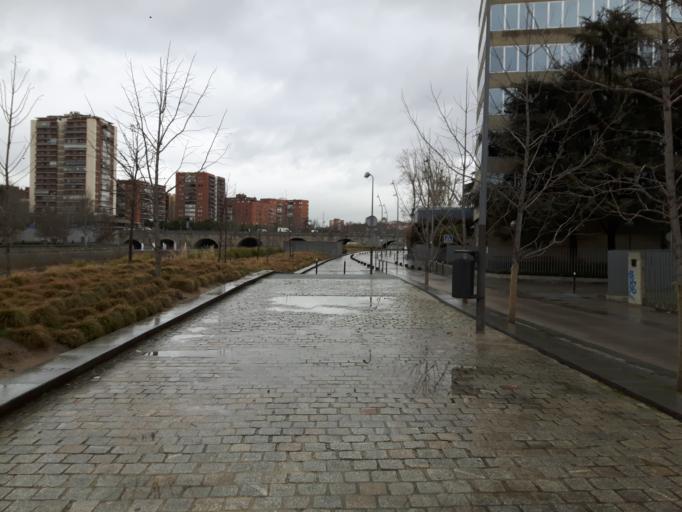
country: ES
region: Madrid
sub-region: Provincia de Madrid
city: Madrid
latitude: 40.4121
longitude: -3.7224
